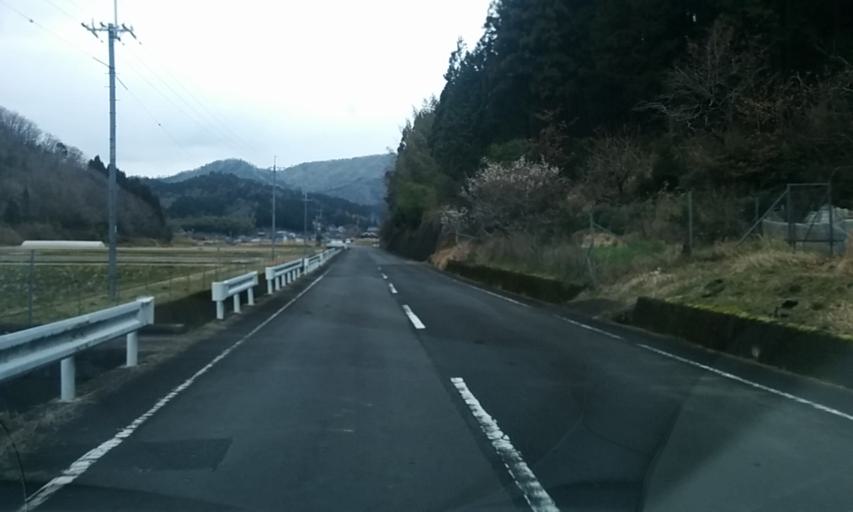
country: JP
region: Kyoto
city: Kameoka
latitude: 35.1217
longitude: 135.4184
